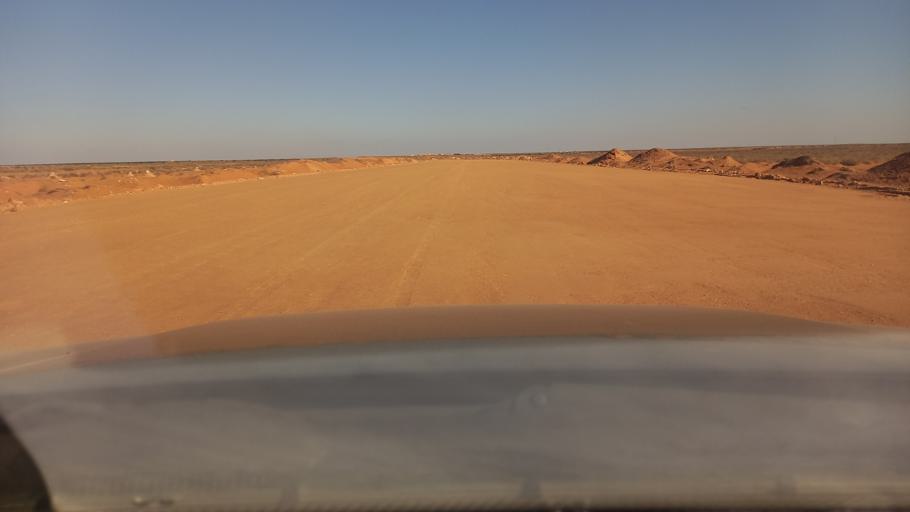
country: TN
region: Madanin
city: Medenine
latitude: 33.1662
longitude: 10.5237
